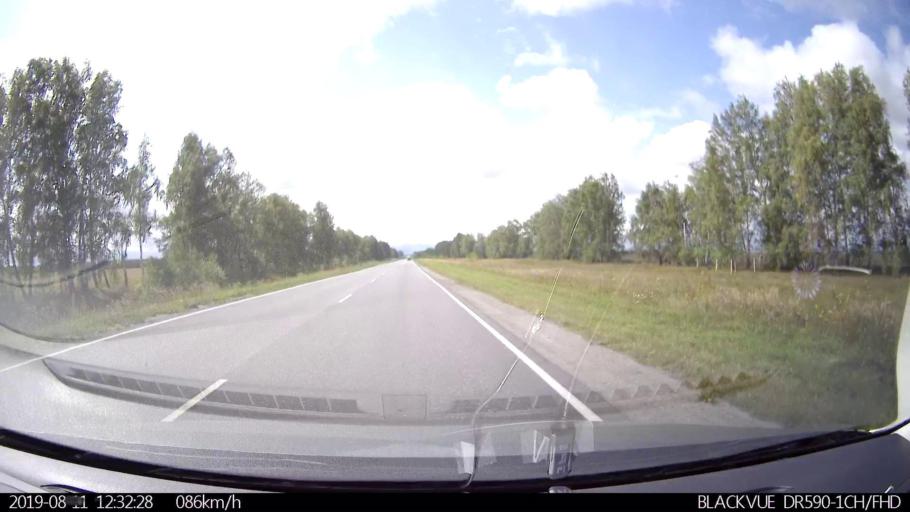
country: RU
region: Ulyanovsk
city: Ignatovka
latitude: 53.8135
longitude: 47.8670
